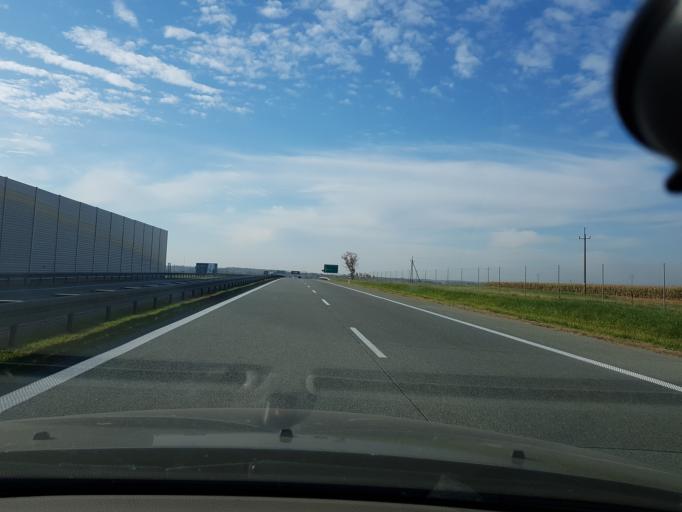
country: PL
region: Lodz Voivodeship
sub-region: Powiat skierniewicki
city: Kowiesy
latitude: 51.8508
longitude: 20.3693
